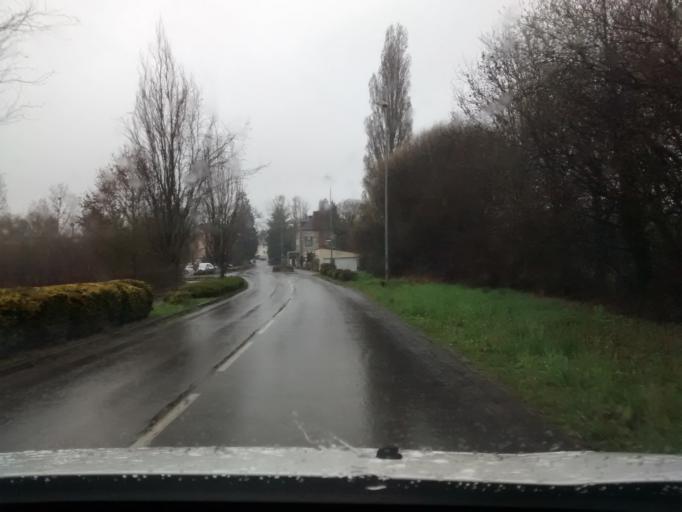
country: FR
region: Brittany
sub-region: Departement d'Ille-et-Vilaine
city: Acigne
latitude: 48.1295
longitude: -1.5339
